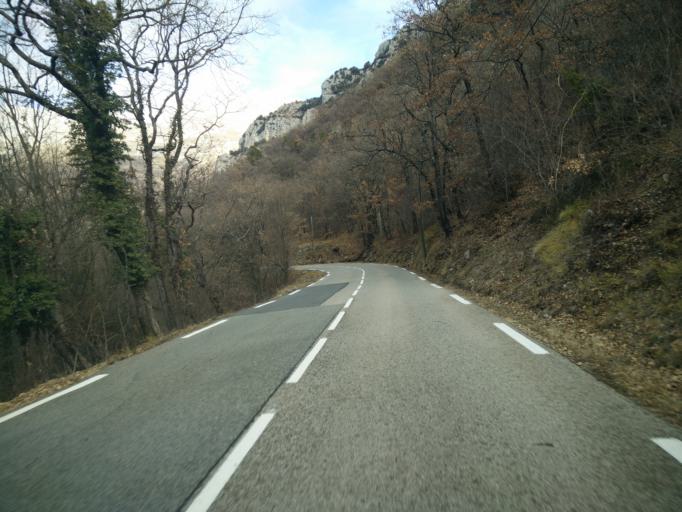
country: FR
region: Provence-Alpes-Cote d'Azur
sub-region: Departement des Alpes-Maritimes
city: Tourrettes-sur-Loup
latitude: 43.7810
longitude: 6.9773
